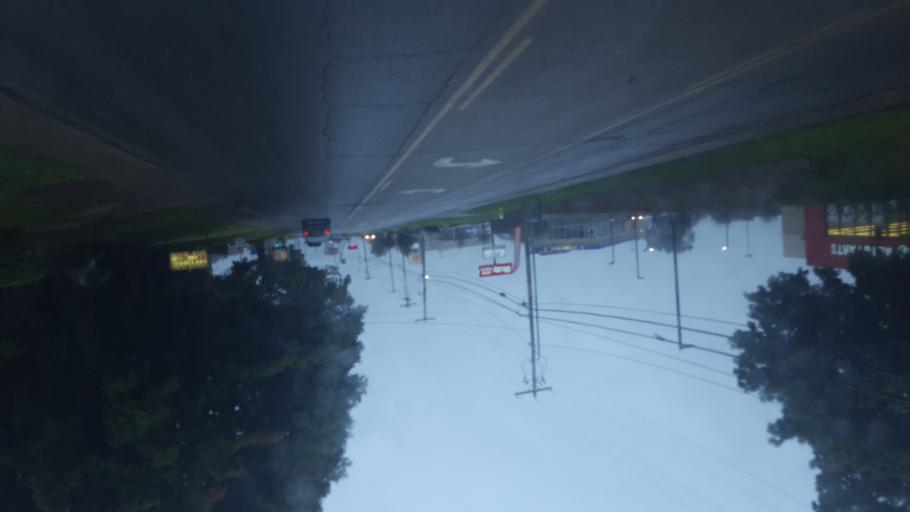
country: US
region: Ohio
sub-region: Jackson County
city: Jackson
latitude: 39.0437
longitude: -82.6296
